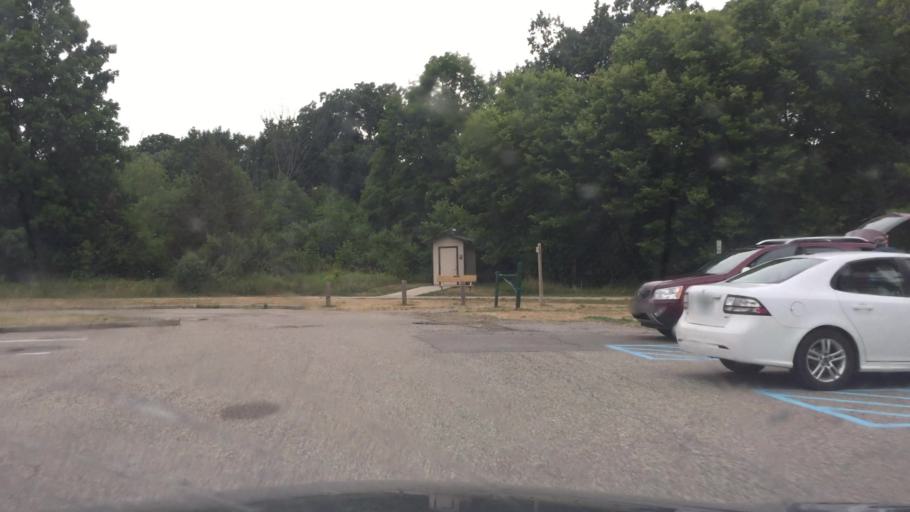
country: US
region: Michigan
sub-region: Oakland County
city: South Lyon
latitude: 42.5119
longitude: -83.6760
